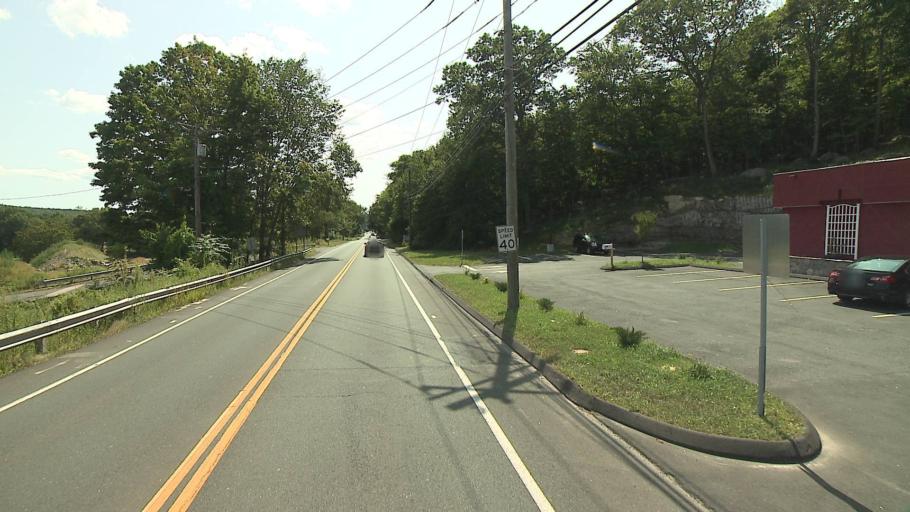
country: US
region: Connecticut
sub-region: Fairfield County
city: Trumbull
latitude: 41.2978
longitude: -73.2476
